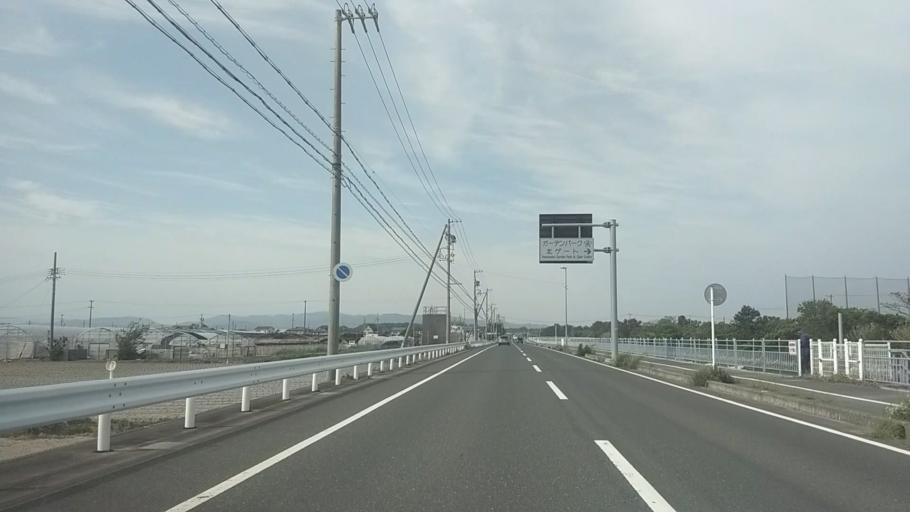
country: JP
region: Shizuoka
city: Kosai-shi
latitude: 34.7134
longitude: 137.5905
